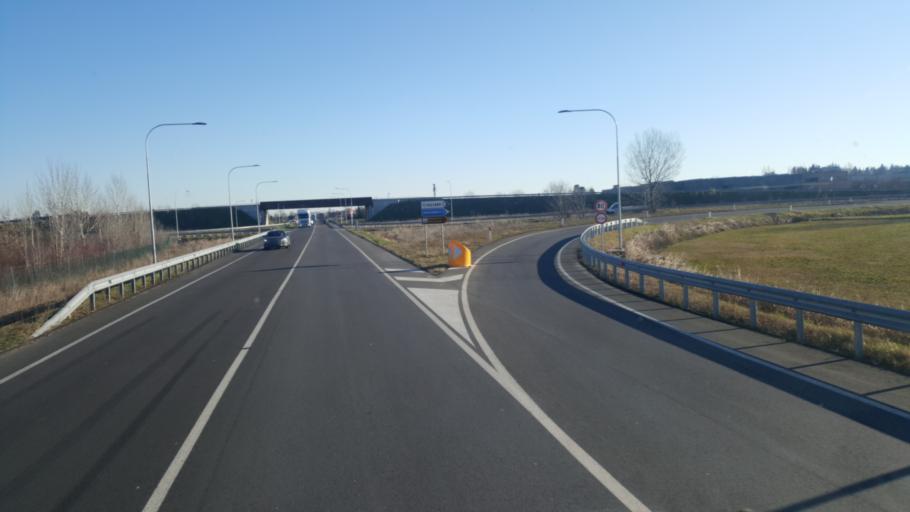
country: IT
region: Emilia-Romagna
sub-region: Provincia di Modena
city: Mulino
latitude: 44.5083
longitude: 11.0630
